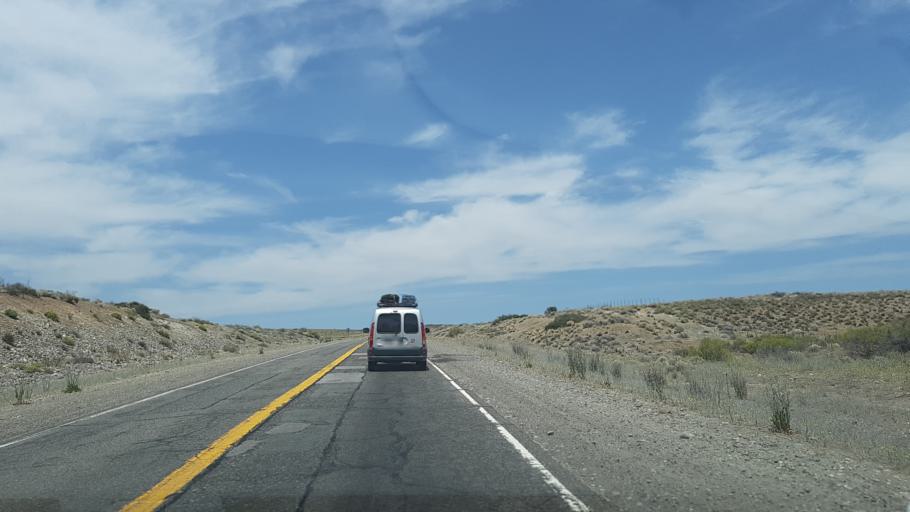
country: AR
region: Rio Negro
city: Pilcaniyeu
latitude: -40.4894
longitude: -70.6800
